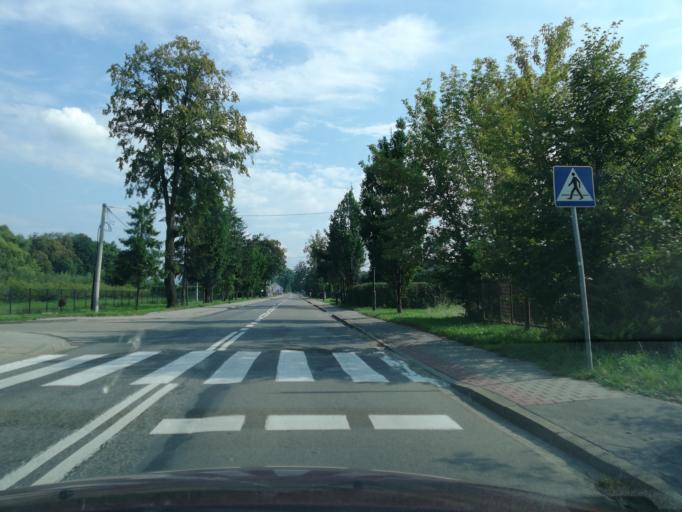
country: PL
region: Lesser Poland Voivodeship
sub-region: Powiat nowosadecki
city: Nawojowa
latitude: 49.5956
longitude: 20.7205
